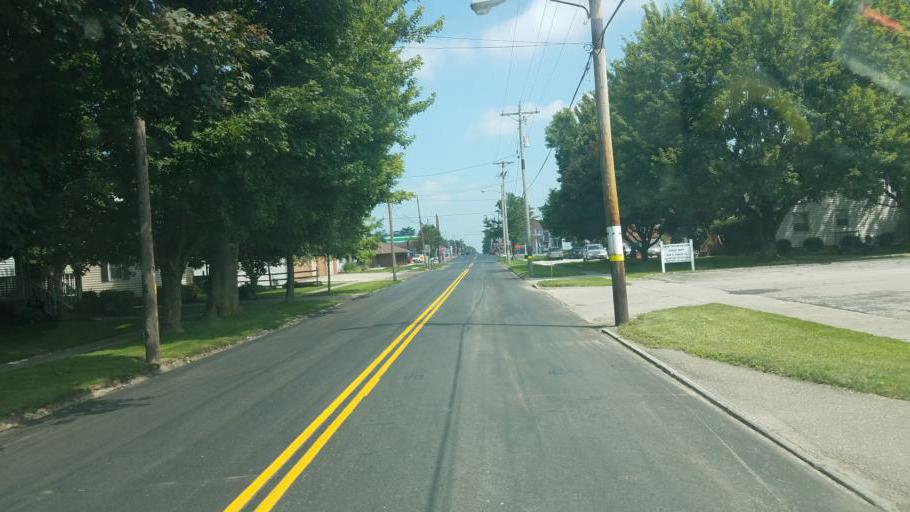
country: US
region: Ohio
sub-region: Huron County
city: Willard
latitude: 40.9599
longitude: -82.8536
